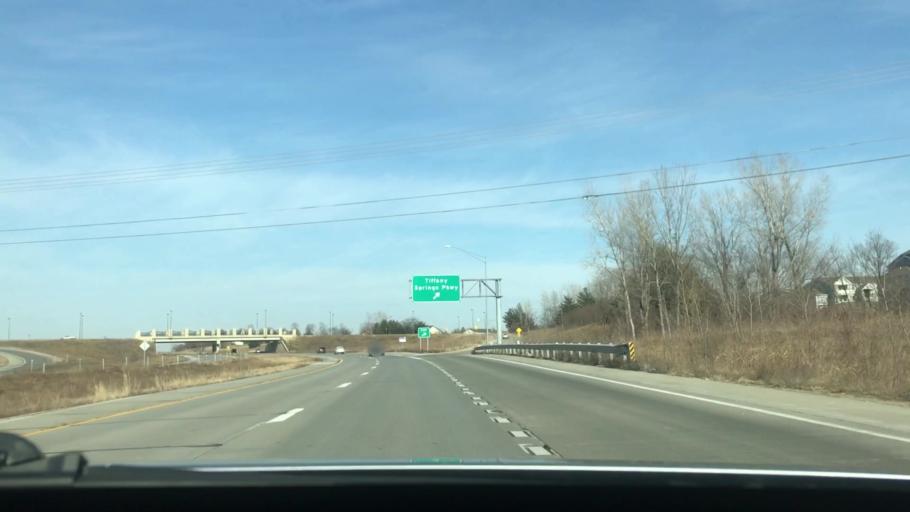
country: US
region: Missouri
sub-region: Clay County
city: Gladstone
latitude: 39.2664
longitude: -94.5851
